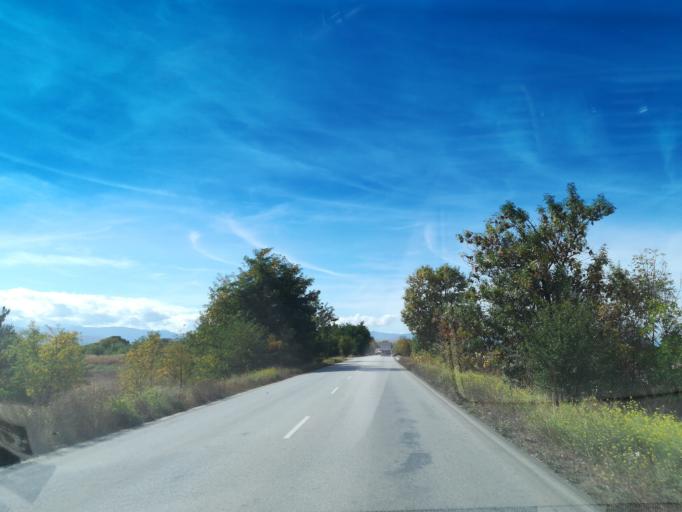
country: BG
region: Plovdiv
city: Stamboliyski
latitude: 42.1191
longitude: 24.5481
